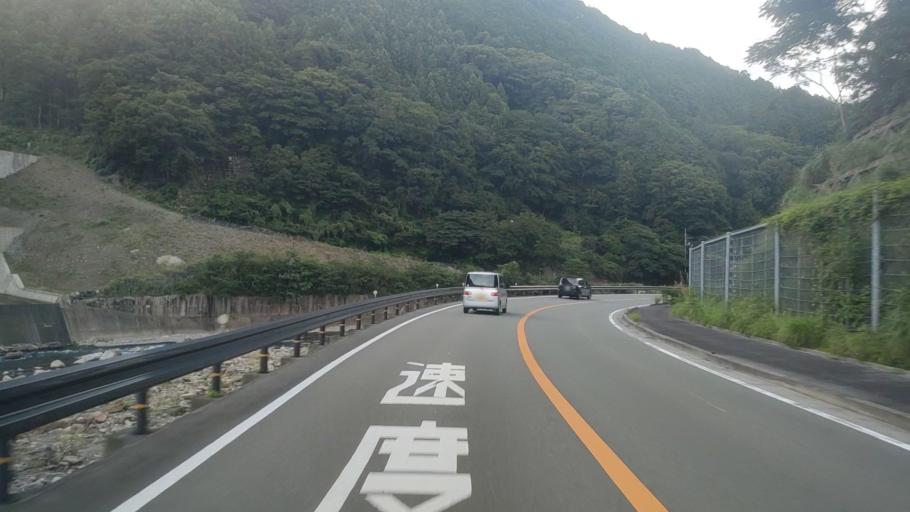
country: JP
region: Wakayama
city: Tanabe
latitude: 33.7728
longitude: 135.5009
